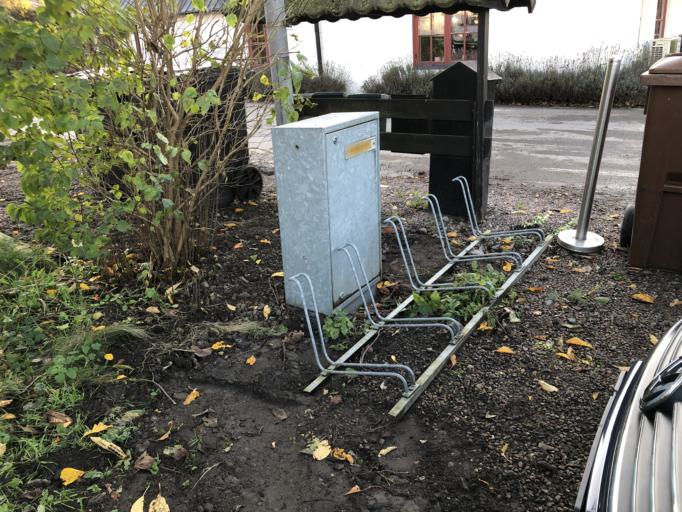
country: SE
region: Skane
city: Smygehamn
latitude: 55.3534
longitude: 13.3149
